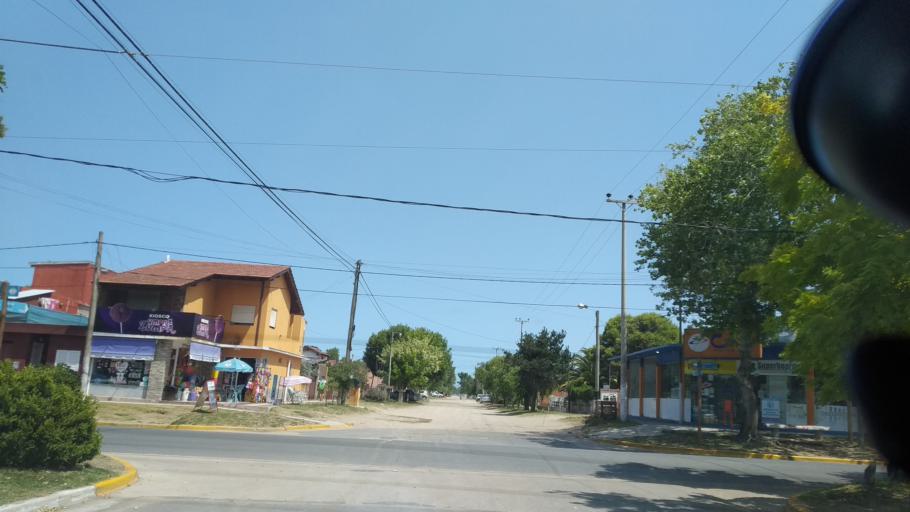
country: AR
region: Buenos Aires
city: Mar del Tuyu
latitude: -36.5813
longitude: -56.6935
